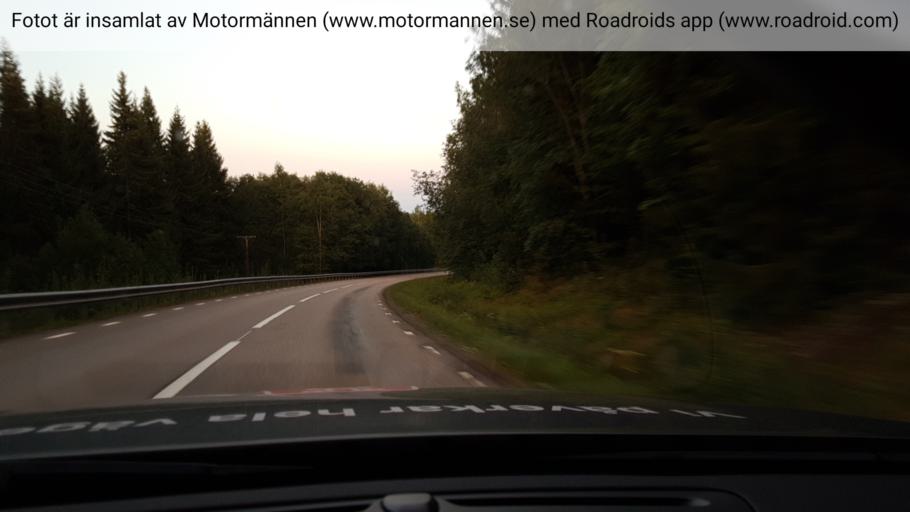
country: SE
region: OErebro
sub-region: Hallefors Kommun
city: Haellefors
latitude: 59.6818
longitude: 14.5140
